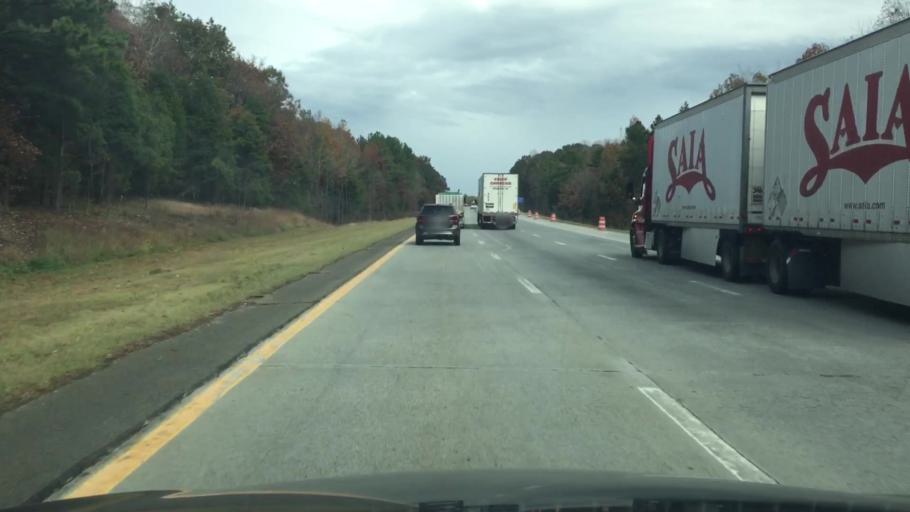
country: US
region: North Carolina
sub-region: Davidson County
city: Thomasville
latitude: 35.8306
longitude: -80.1557
